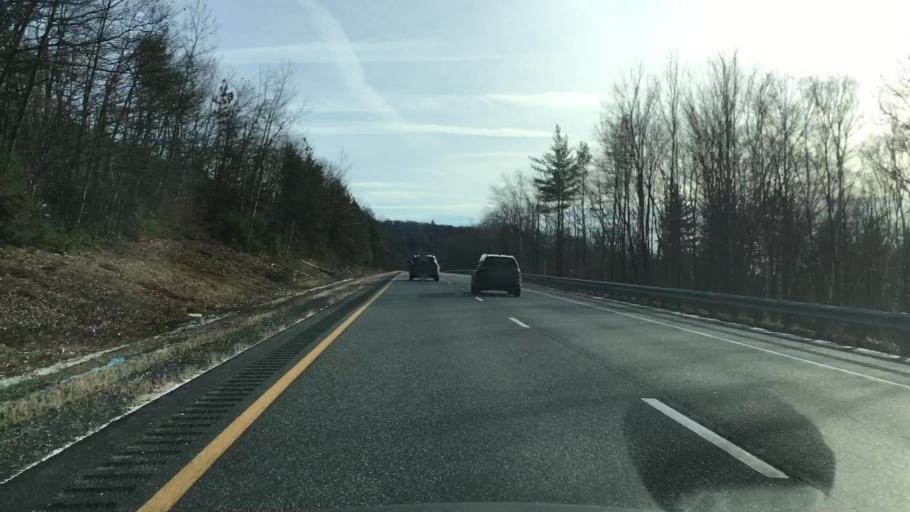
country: US
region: New Hampshire
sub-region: Sullivan County
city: Grantham
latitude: 43.4826
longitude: -72.1044
